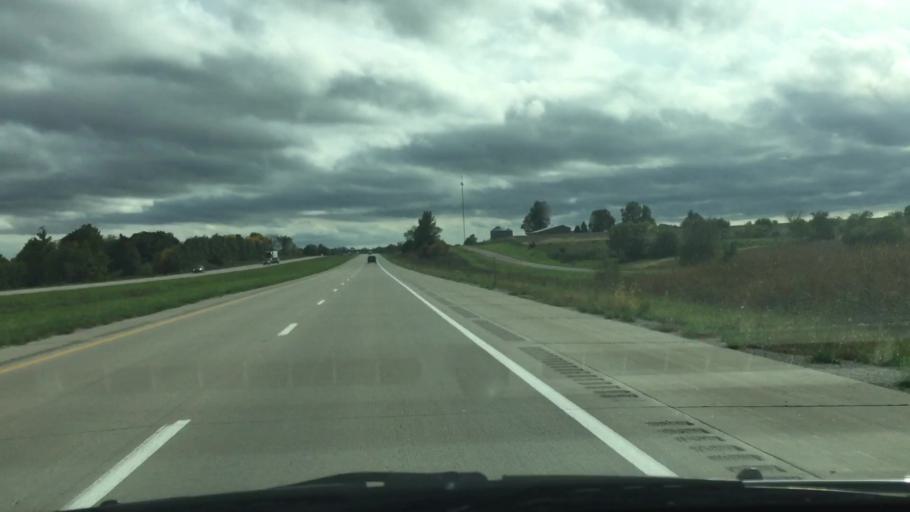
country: US
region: Iowa
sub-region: Decatur County
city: Leon
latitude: 40.7725
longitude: -93.8362
